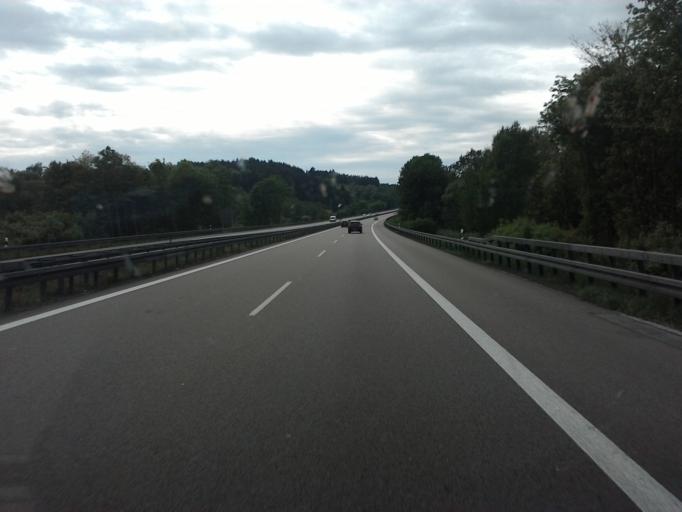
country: DE
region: Bavaria
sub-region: Upper Palatinate
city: Velburg
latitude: 49.2462
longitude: 11.6246
